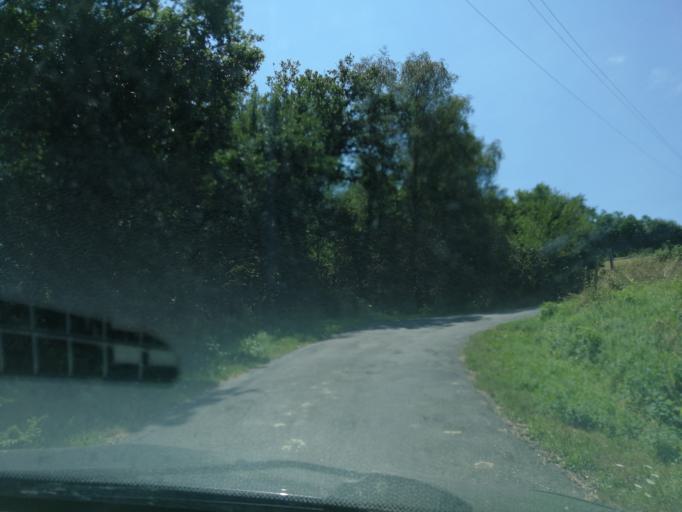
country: FR
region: Auvergne
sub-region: Departement du Cantal
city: Maurs
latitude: 44.6826
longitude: 2.3260
